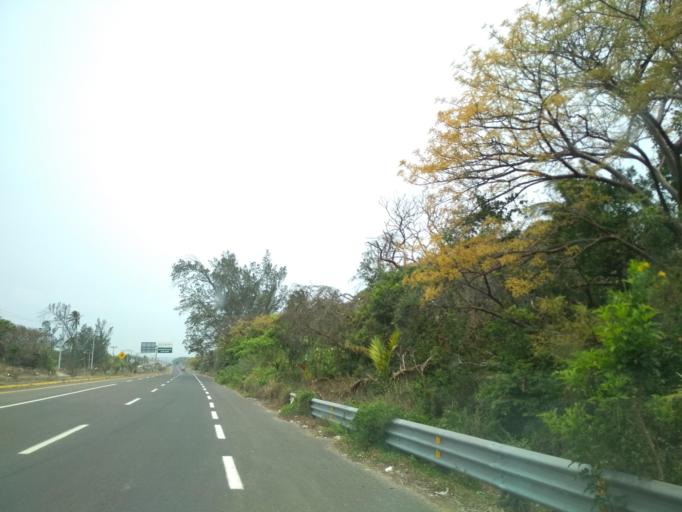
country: MX
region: Veracruz
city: Anton Lizardo
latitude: 19.0519
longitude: -96.0162
